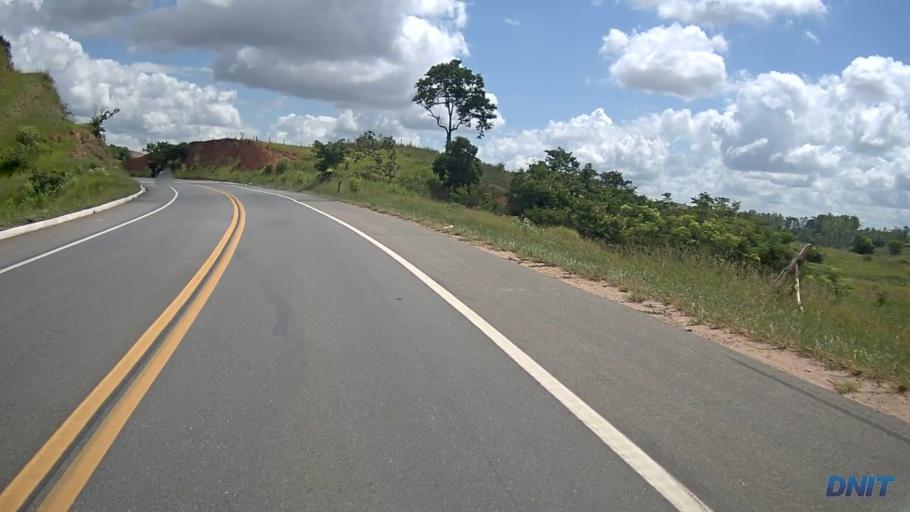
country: BR
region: Minas Gerais
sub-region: Governador Valadares
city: Governador Valadares
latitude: -18.9060
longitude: -42.0037
